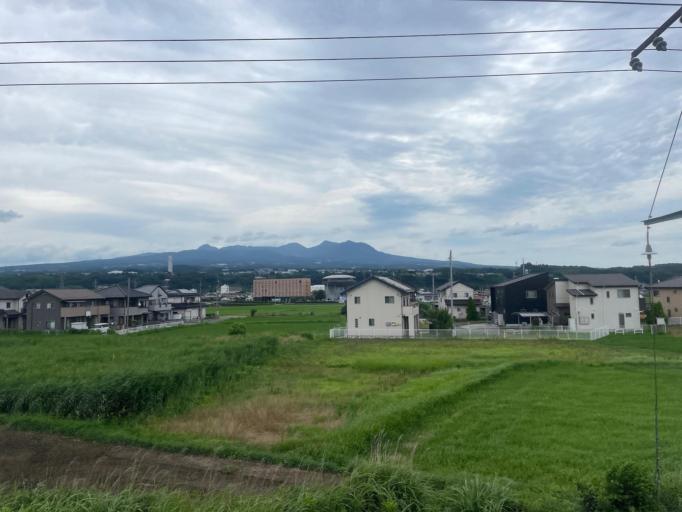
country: JP
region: Gunma
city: Shibukawa
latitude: 36.4687
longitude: 139.0181
